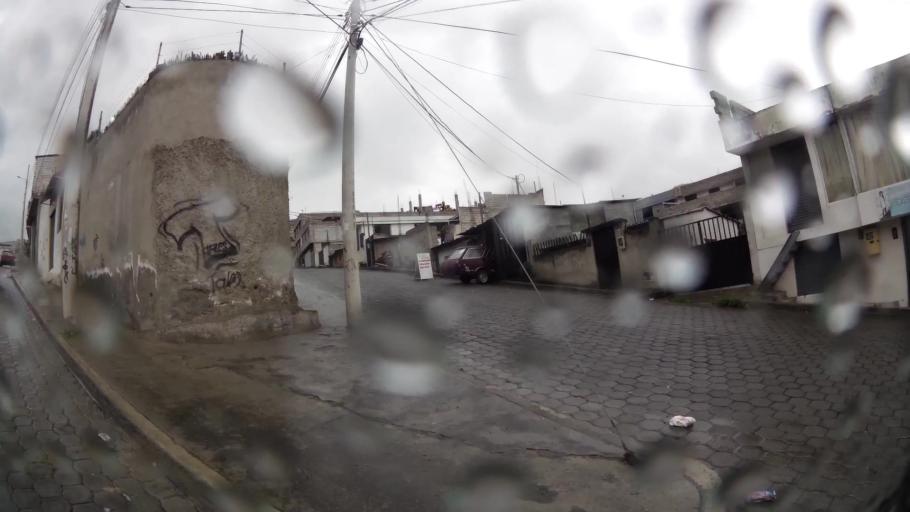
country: EC
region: Pichincha
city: Quito
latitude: -0.0934
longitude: -78.5009
